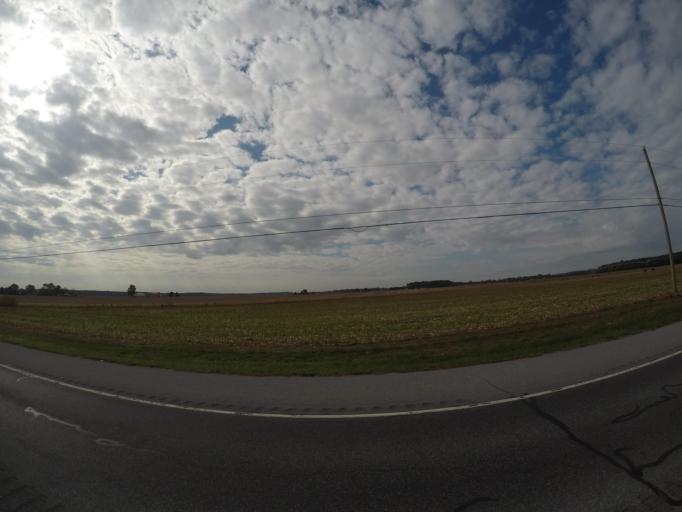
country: US
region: Delaware
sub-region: Sussex County
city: Bridgeville
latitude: 38.7126
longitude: -75.5697
